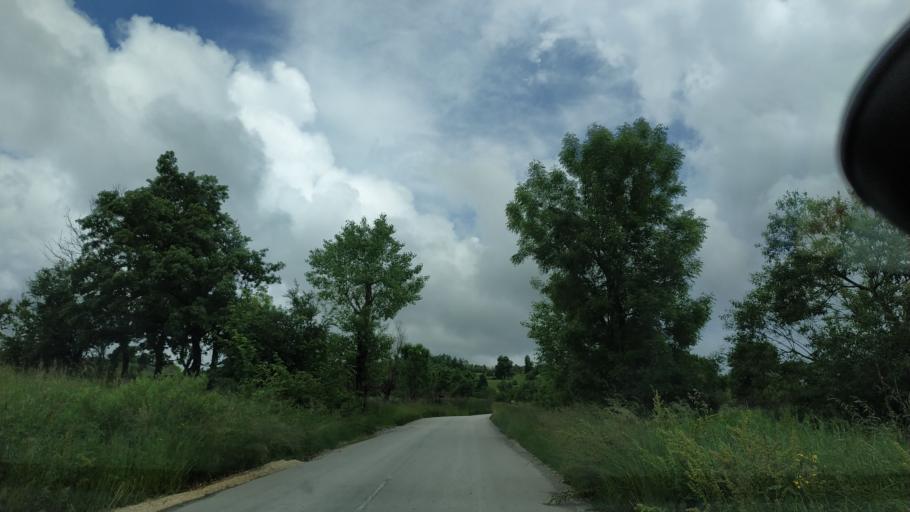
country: RS
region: Central Serbia
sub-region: Zajecarski Okrug
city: Soko Banja
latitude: 43.6820
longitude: 21.9333
